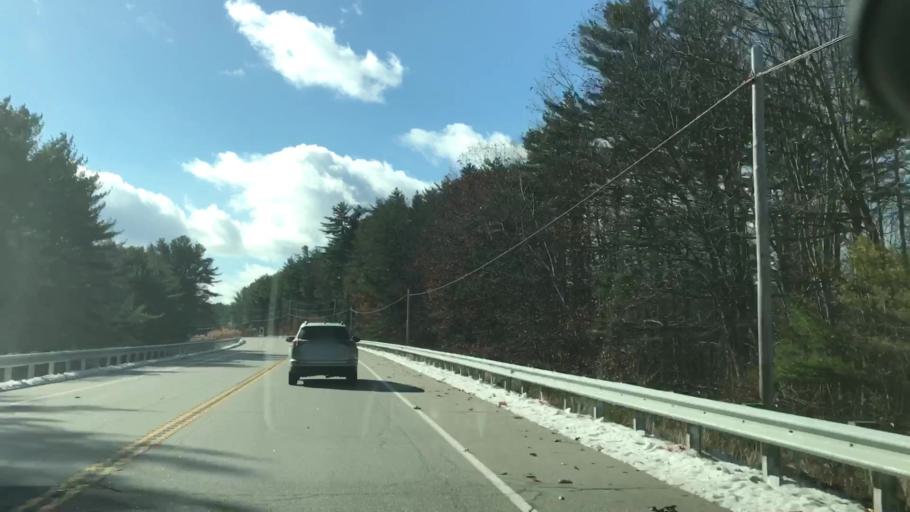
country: US
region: New Hampshire
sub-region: Carroll County
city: Ossipee
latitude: 43.6903
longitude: -71.1189
